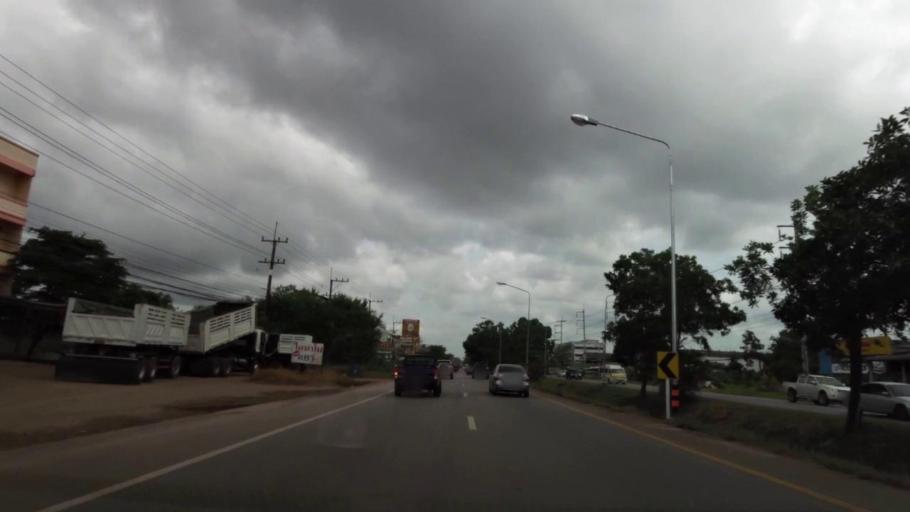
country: TH
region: Chanthaburi
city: Na Yai Am
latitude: 12.7805
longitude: 101.8189
